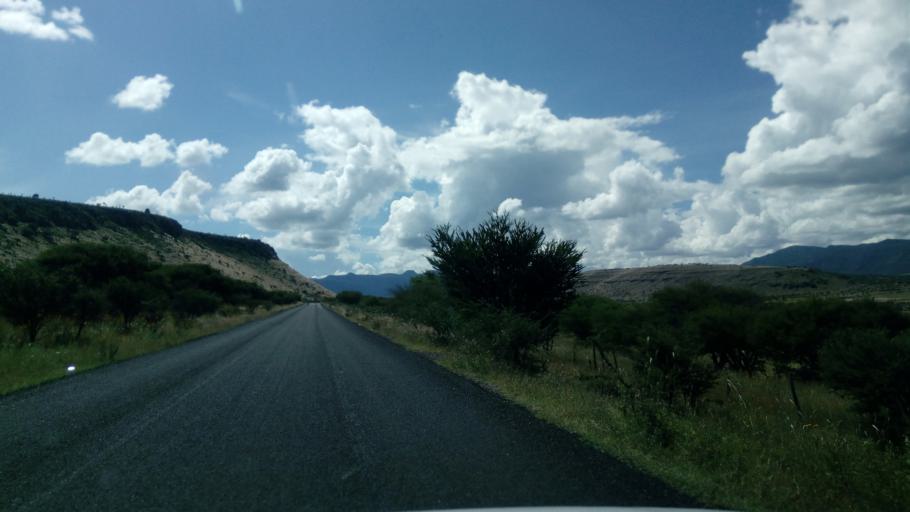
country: MX
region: Durango
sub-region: Durango
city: Jose Refugio Salcido
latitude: 23.8386
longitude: -104.4807
